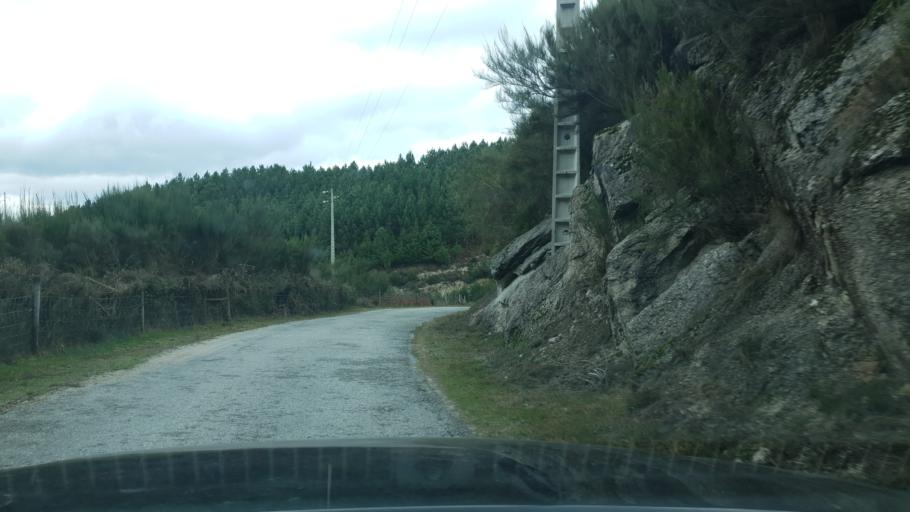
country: PT
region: Viseu
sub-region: Castro Daire
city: Castro Daire
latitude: 40.8779
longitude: -7.9899
